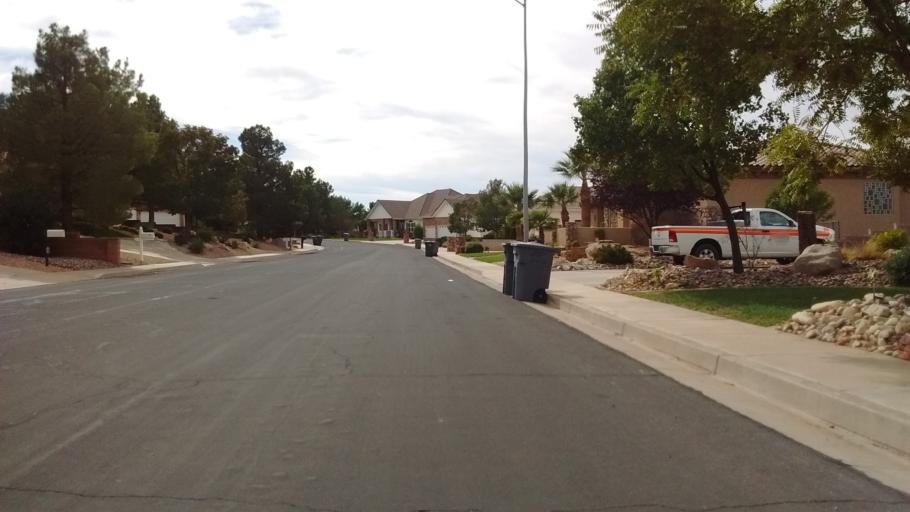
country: US
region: Utah
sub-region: Washington County
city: Washington
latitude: 37.1213
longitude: -113.4943
